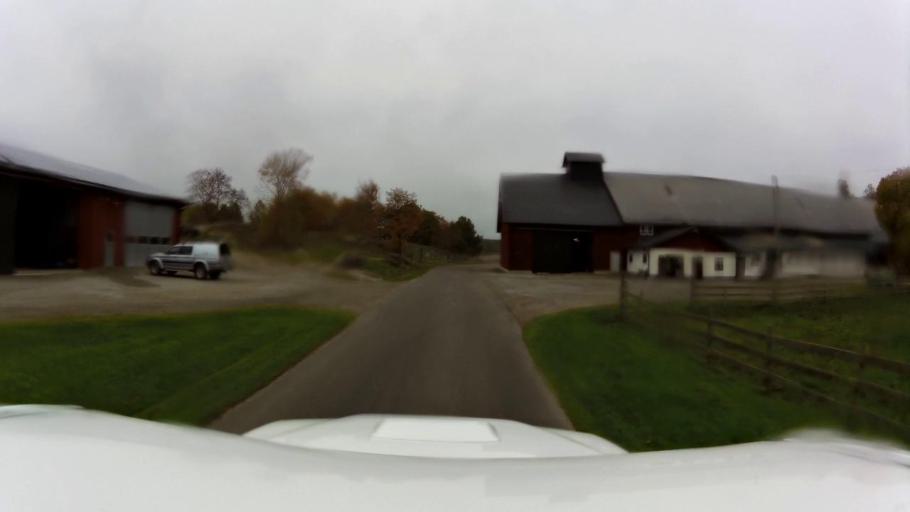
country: SE
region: OEstergoetland
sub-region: Linkopings Kommun
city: Linghem
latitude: 58.3516
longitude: 15.8927
